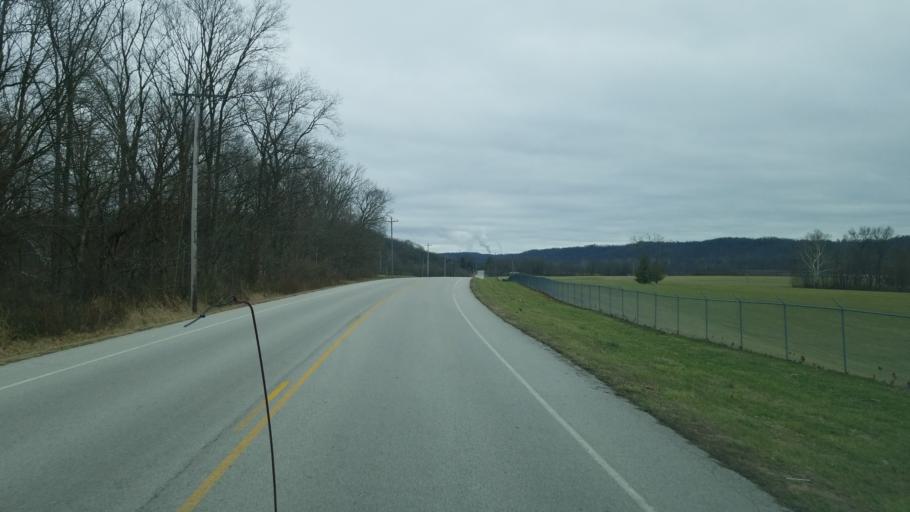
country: US
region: Kentucky
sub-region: Bracken County
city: Augusta
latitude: 38.7800
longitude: -83.9235
